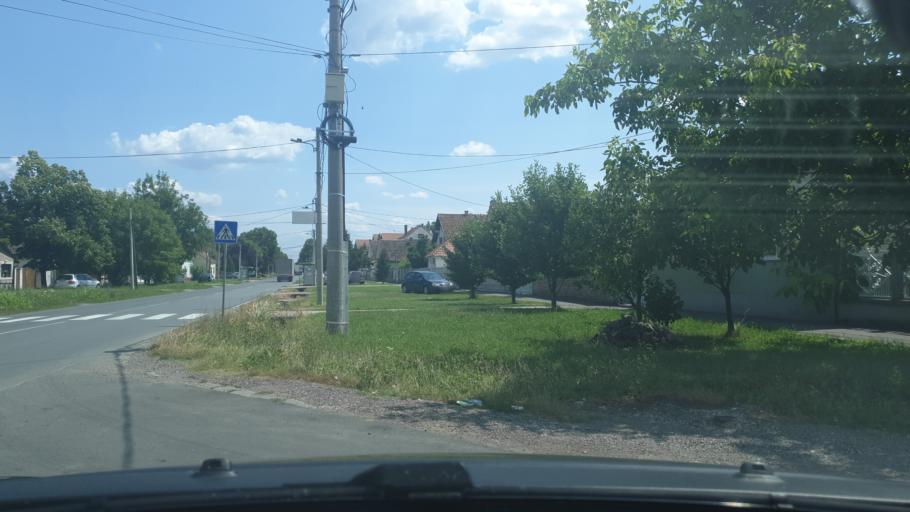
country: RS
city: Dobanovci
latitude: 44.8386
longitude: 20.2148
